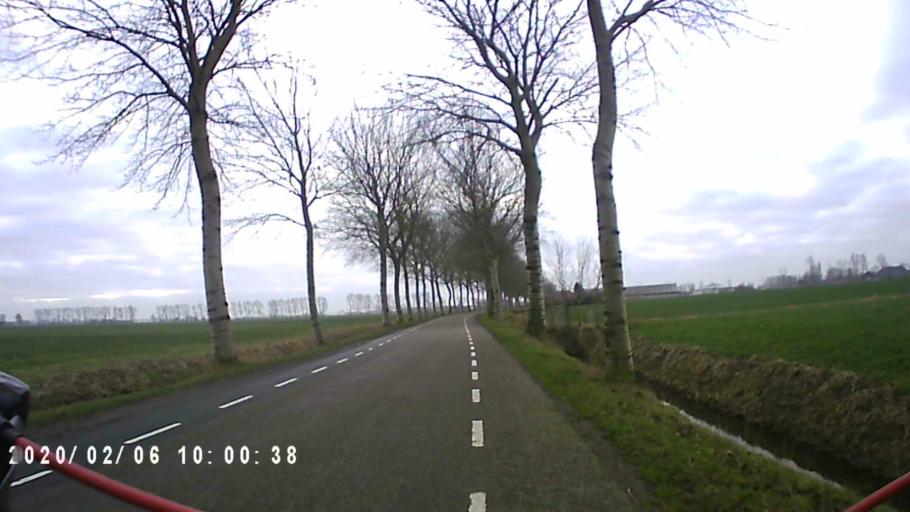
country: NL
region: Groningen
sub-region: Gemeente Zuidhorn
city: Aduard
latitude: 53.2653
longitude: 6.4907
